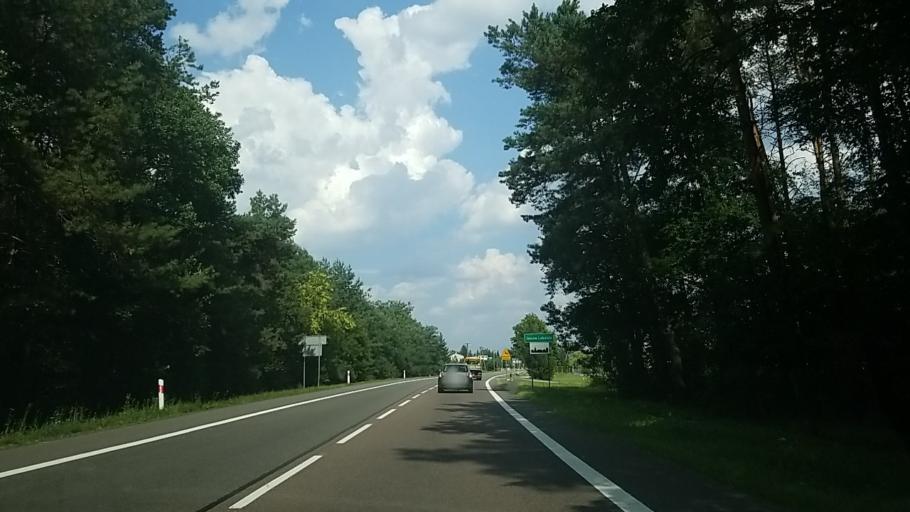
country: PL
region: Lublin Voivodeship
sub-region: Powiat janowski
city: Janow Lubelski
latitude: 50.6925
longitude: 22.3761
